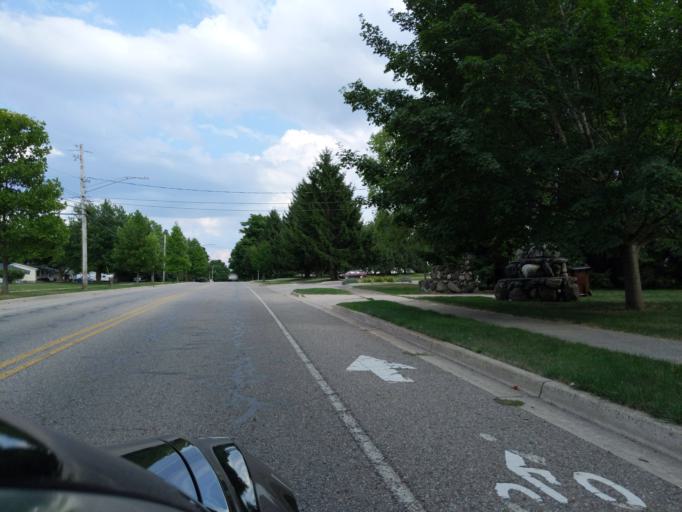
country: US
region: Michigan
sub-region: Clinton County
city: DeWitt
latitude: 42.8360
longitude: -84.5616
